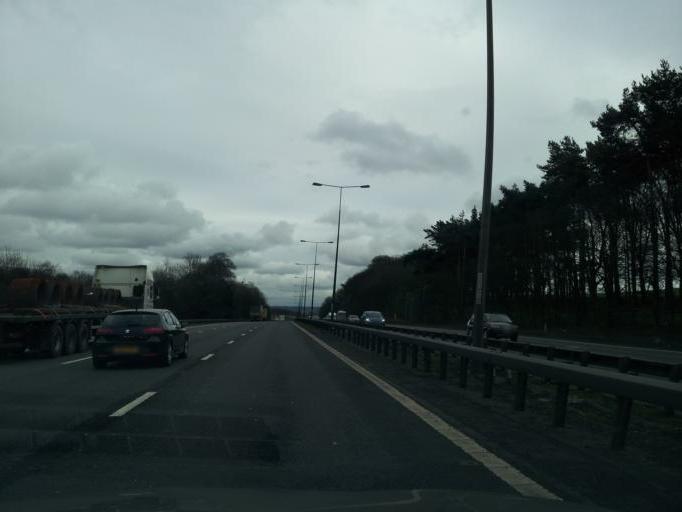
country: GB
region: England
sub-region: Staffordshire
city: Newcastle under Lyme
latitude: 52.9913
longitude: -2.2715
